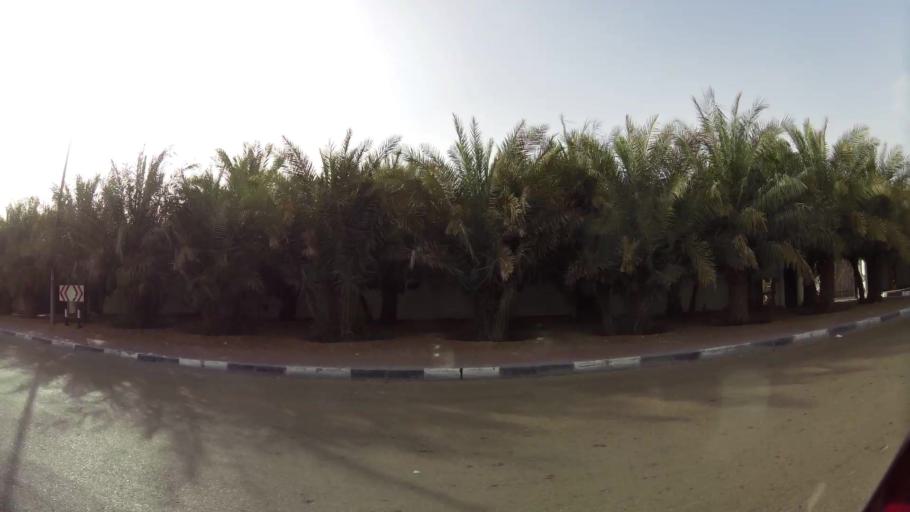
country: AE
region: Abu Dhabi
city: Al Ain
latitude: 24.2105
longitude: 55.6344
